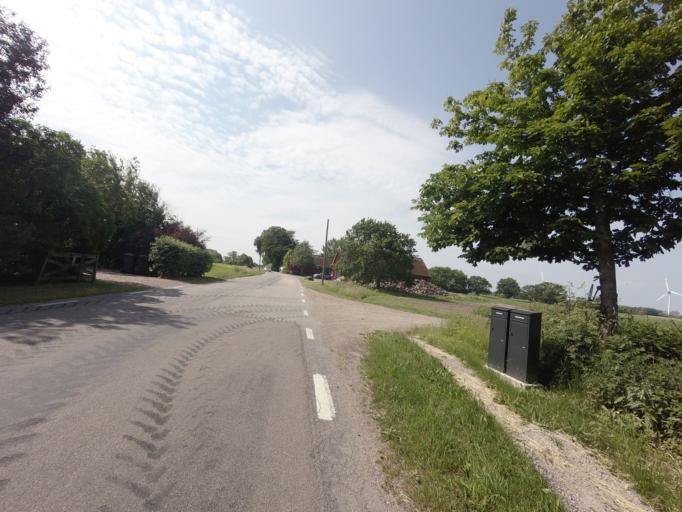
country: SE
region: Skane
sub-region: Helsingborg
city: Odakra
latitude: 56.2036
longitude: 12.7032
